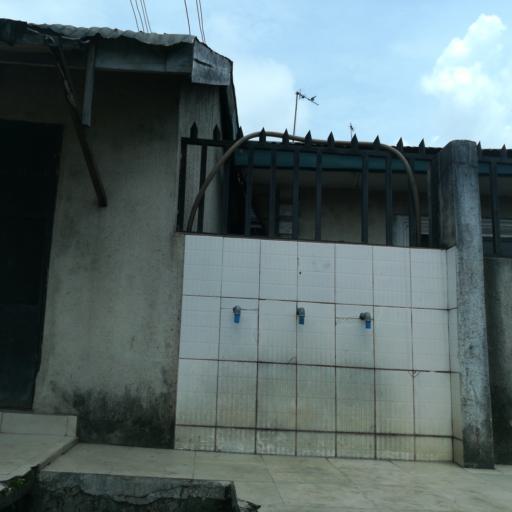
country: NG
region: Rivers
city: Port Harcourt
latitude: 4.7791
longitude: 7.0357
